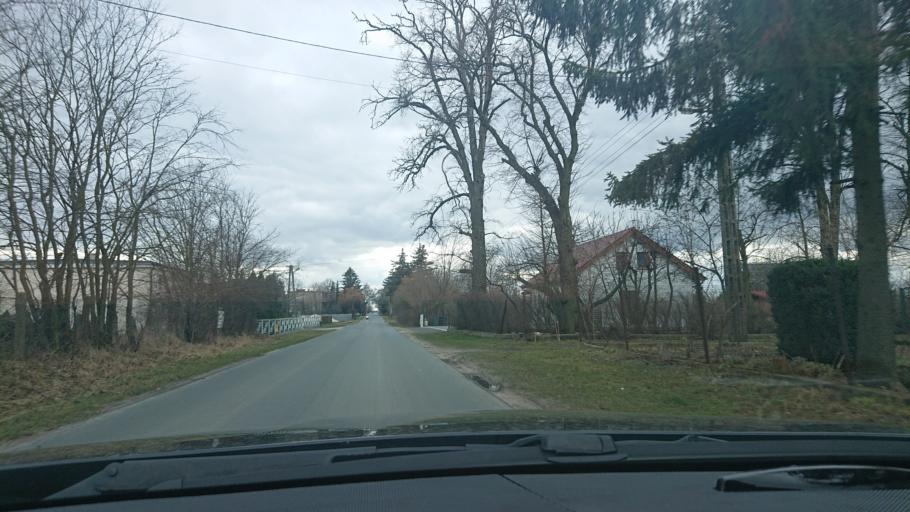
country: PL
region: Greater Poland Voivodeship
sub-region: Powiat gnieznienski
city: Gniezno
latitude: 52.5761
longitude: 17.6268
